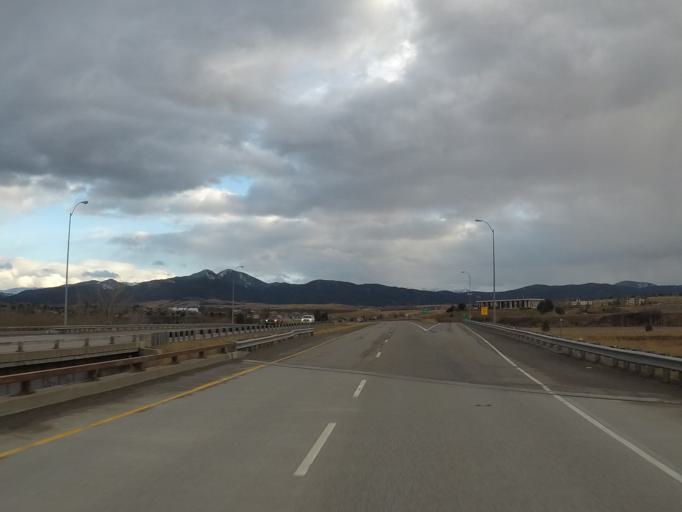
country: US
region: Montana
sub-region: Gallatin County
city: Bozeman
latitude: 45.6794
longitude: -111.0122
